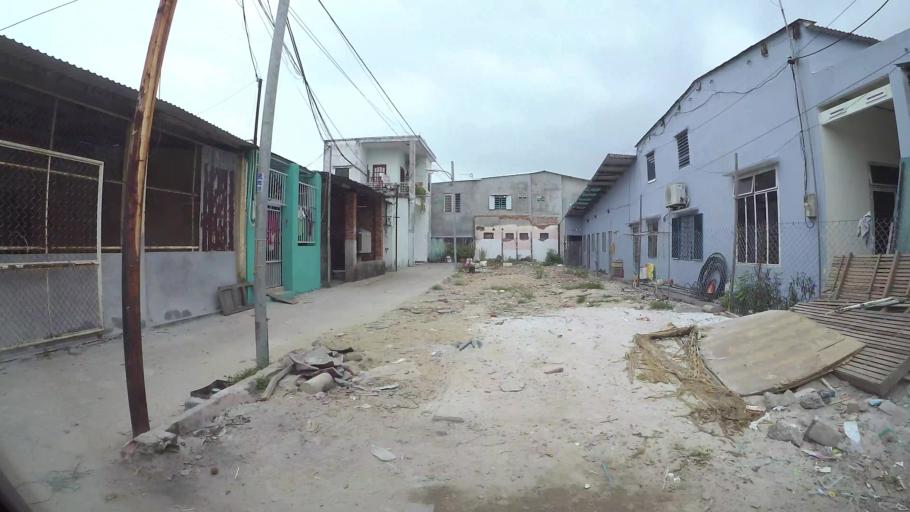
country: VN
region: Da Nang
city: Lien Chieu
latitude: 16.0714
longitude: 108.1526
